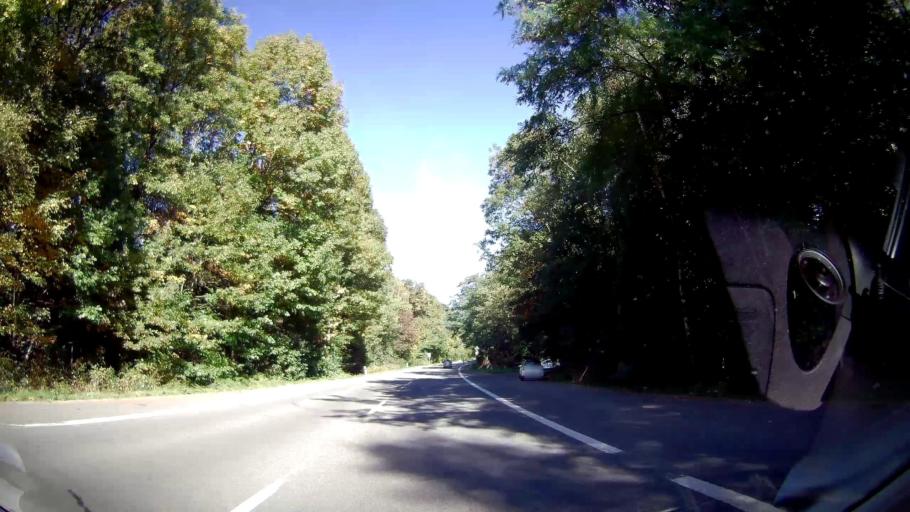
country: DE
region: North Rhine-Westphalia
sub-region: Regierungsbezirk Dusseldorf
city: Hunxe
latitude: 51.6022
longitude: 6.8254
